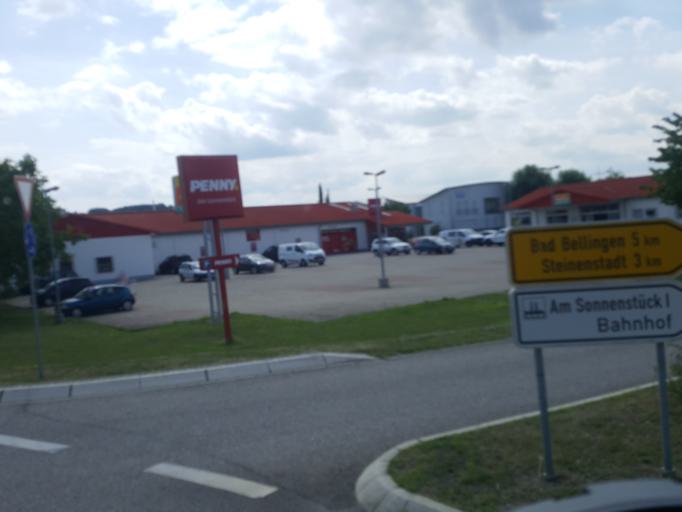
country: DE
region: Baden-Wuerttemberg
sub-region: Freiburg Region
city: Schliengen
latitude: 47.7643
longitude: 7.5785
